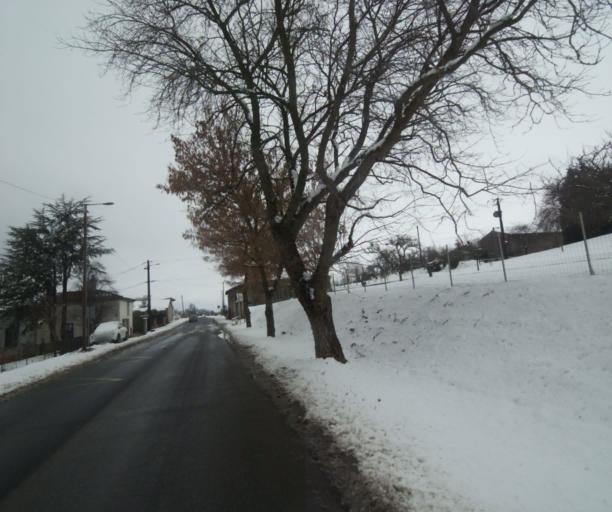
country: FR
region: Champagne-Ardenne
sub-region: Departement de la Haute-Marne
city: Wassy
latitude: 48.4468
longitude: 4.9568
